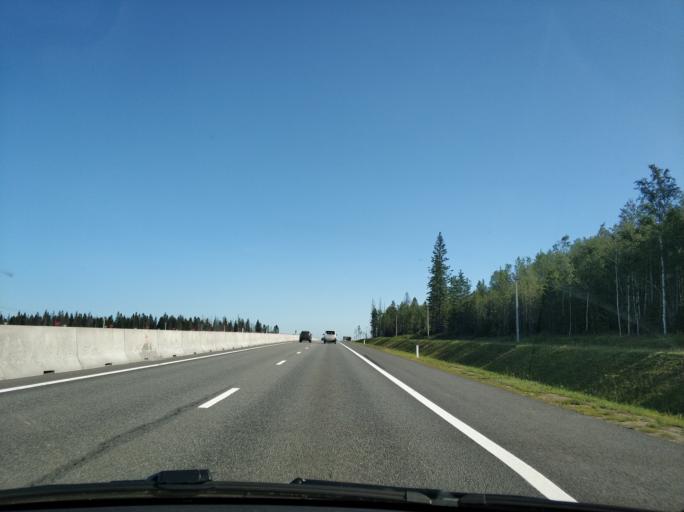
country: RU
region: Leningrad
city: Sosnovo
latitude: 60.4889
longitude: 30.1958
